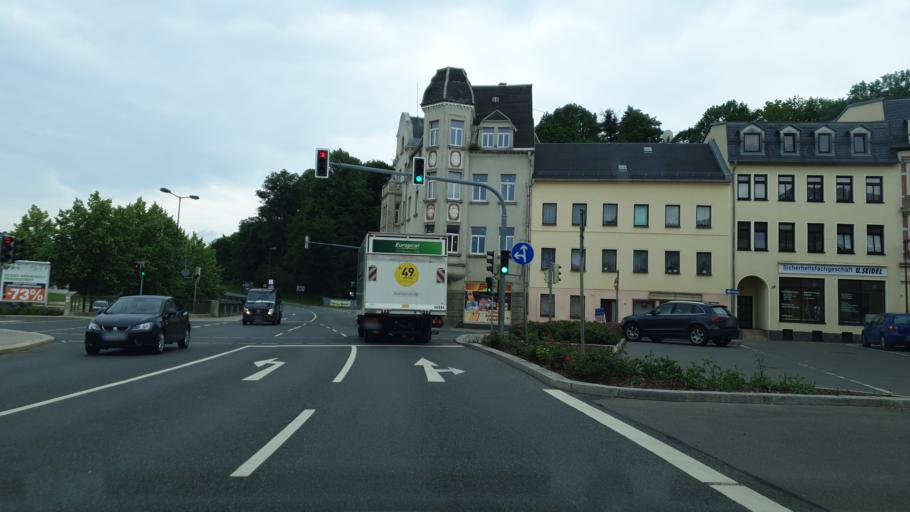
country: DE
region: Saxony
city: Auerbach
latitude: 50.5094
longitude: 12.3978
